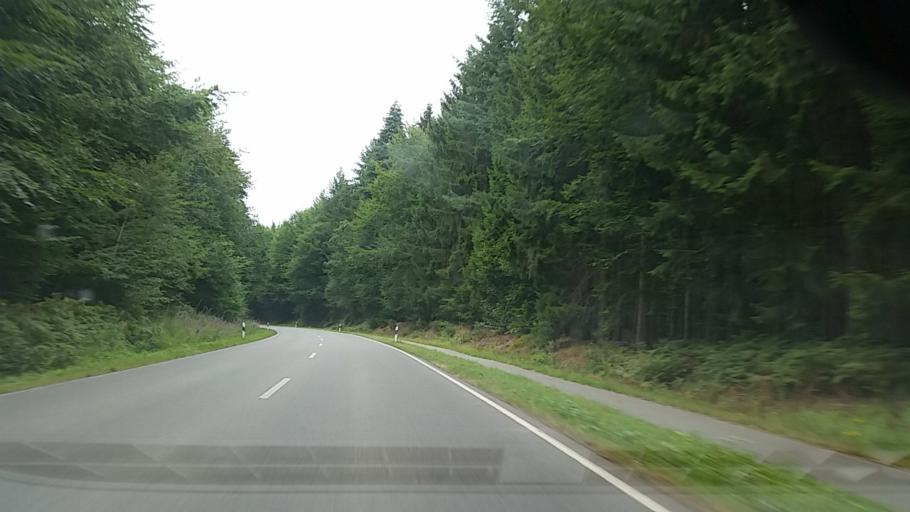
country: DE
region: Schleswig-Holstein
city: Dassendorf
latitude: 53.5155
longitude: 10.3542
